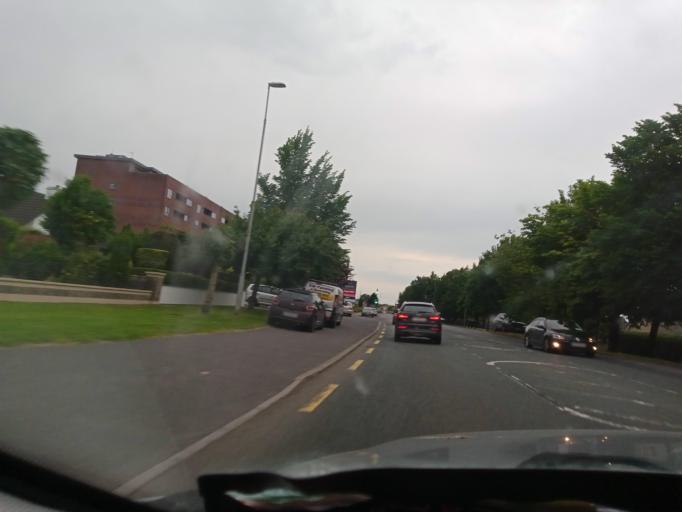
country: IE
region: Leinster
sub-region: Laois
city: Portlaoise
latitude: 53.0247
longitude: -7.2994
